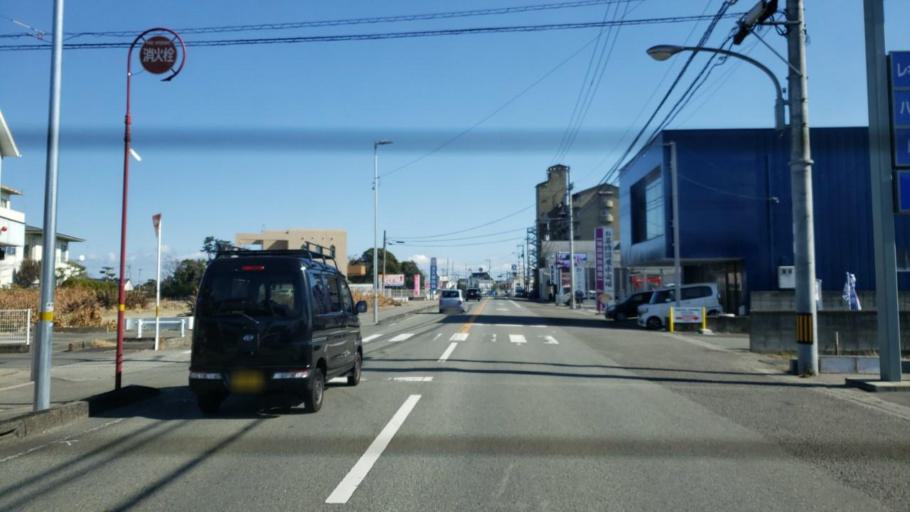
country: JP
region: Tokushima
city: Tokushima-shi
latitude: 34.1320
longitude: 134.5203
